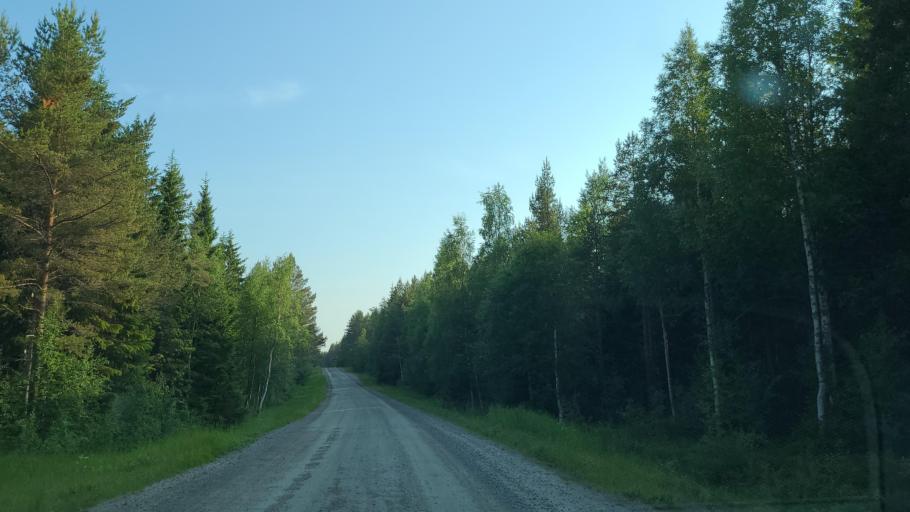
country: SE
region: Vaesterbotten
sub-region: Skelleftea Kommun
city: Burea
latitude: 64.3826
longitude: 21.4610
